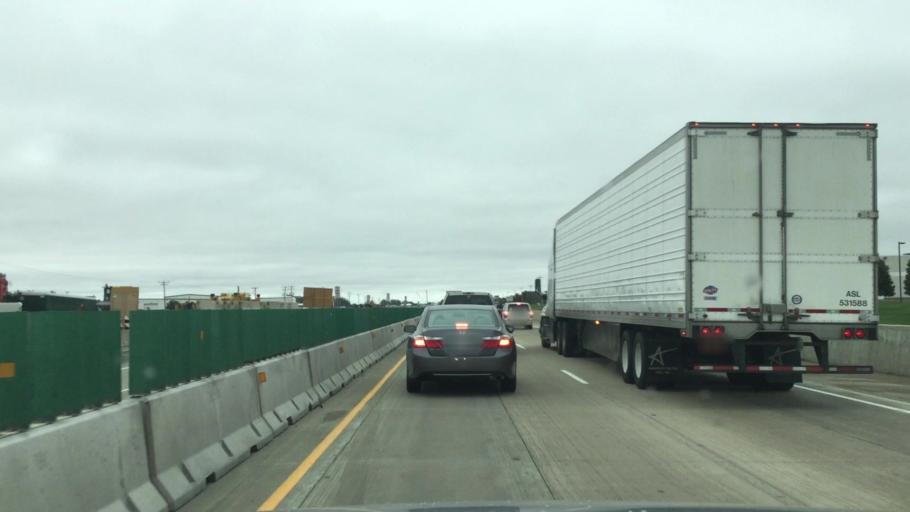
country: US
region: Wisconsin
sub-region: Racine County
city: Franksville
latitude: 42.7175
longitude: -87.9540
